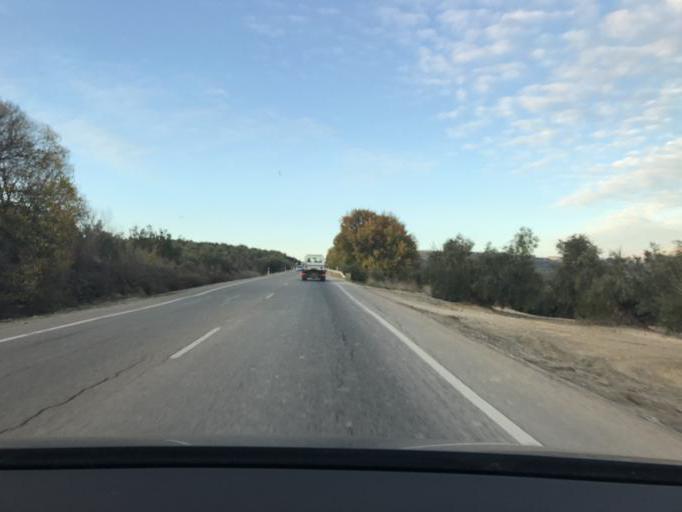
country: ES
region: Andalusia
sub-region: Provincia de Jaen
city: Ubeda
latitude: 37.9815
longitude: -3.3807
